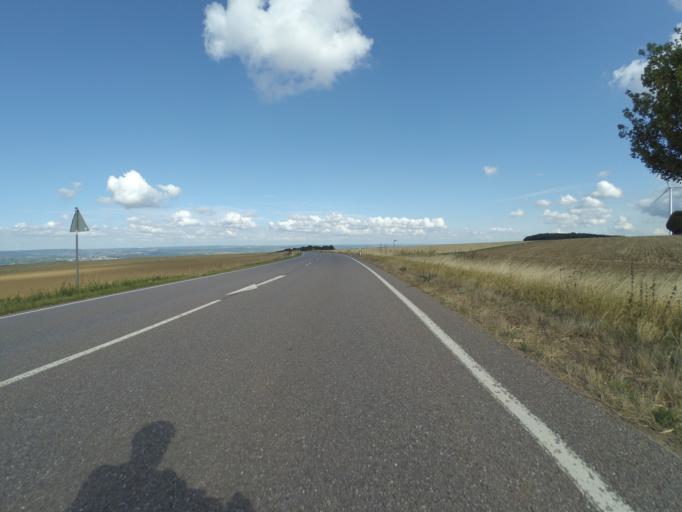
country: DE
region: Rheinland-Pfalz
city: Kirf
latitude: 49.5197
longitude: 6.4456
